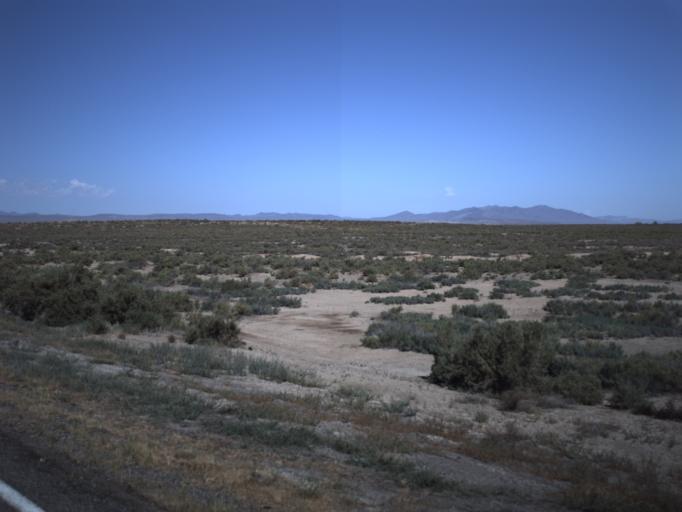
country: US
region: Utah
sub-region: Millard County
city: Delta
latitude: 39.3309
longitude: -112.7152
